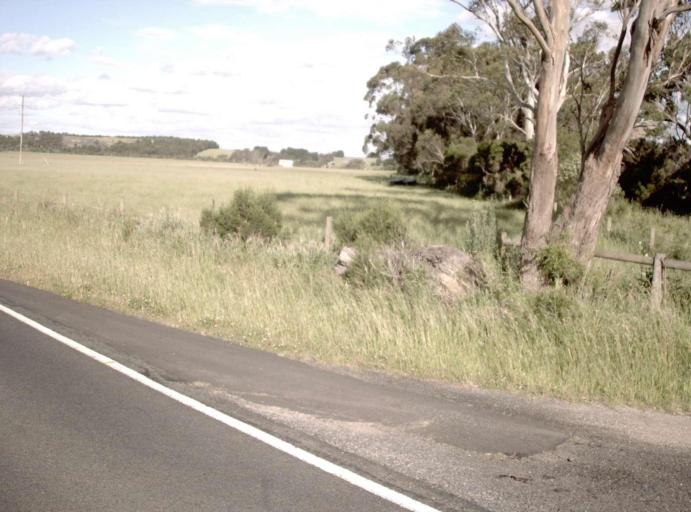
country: AU
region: Victoria
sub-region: Bass Coast
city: North Wonthaggi
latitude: -38.5272
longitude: 145.8850
